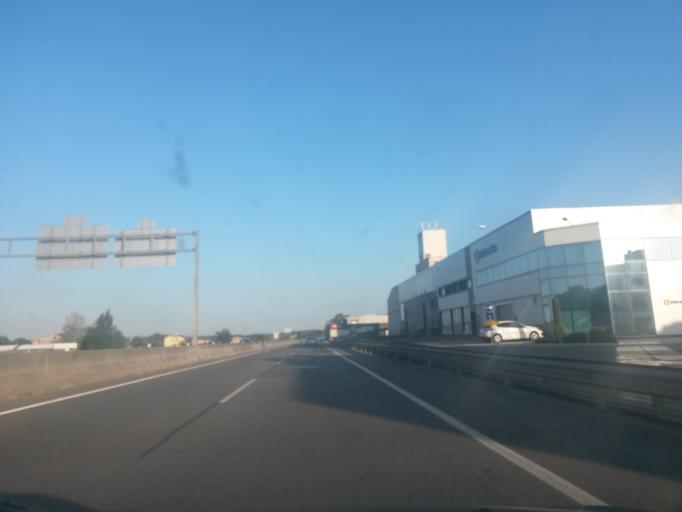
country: ES
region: Catalonia
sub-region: Provincia de Girona
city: Cornella del Terri
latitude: 42.0936
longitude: 2.8032
